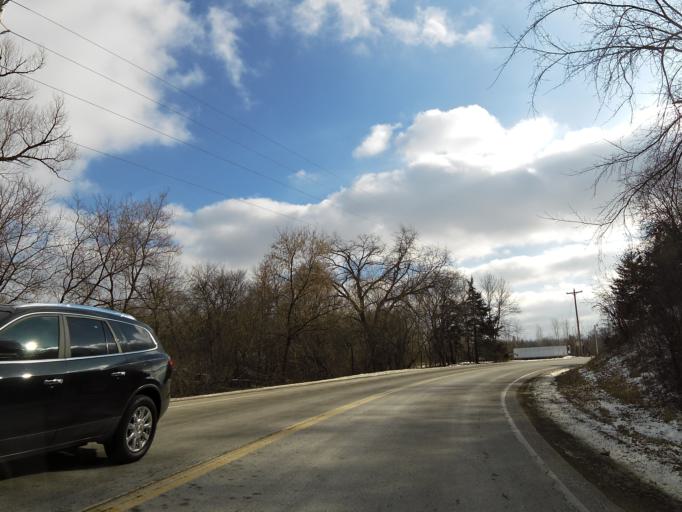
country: US
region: Minnesota
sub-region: Hennepin County
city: Eden Prairie
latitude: 44.8198
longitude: -93.4807
